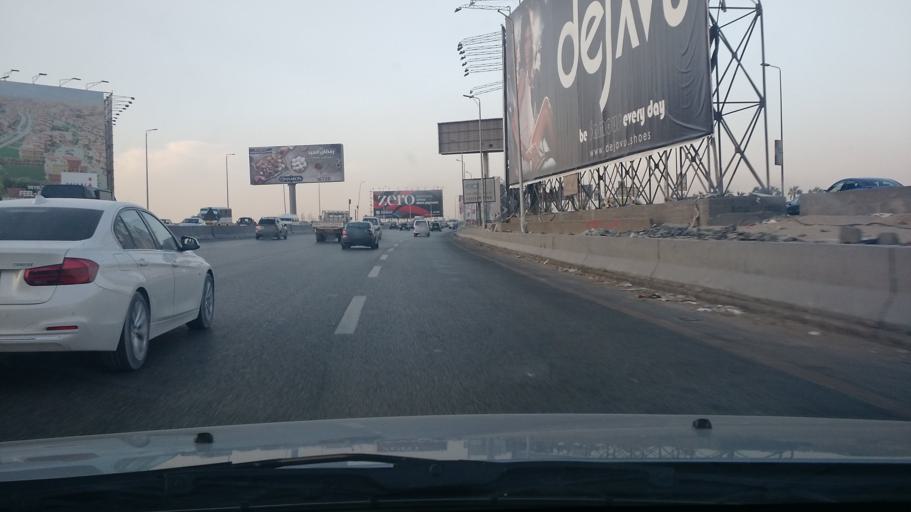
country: EG
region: Muhafazat al Qahirah
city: Cairo
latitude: 29.9850
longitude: 31.3671
